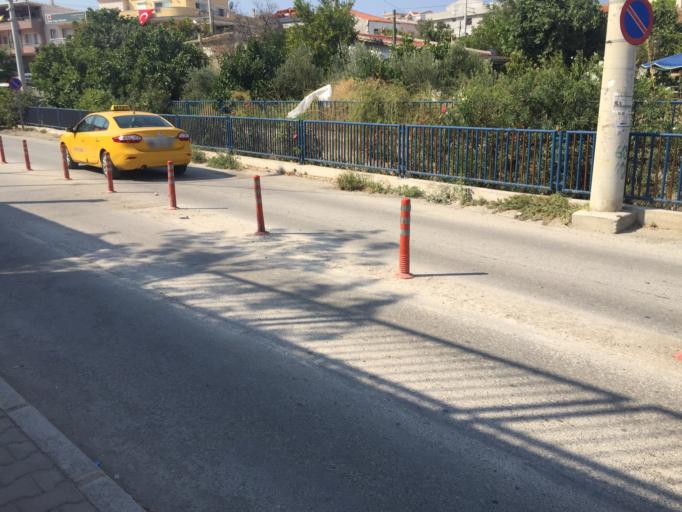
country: TR
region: Izmir
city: Urla
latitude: 38.3247
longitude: 26.7645
